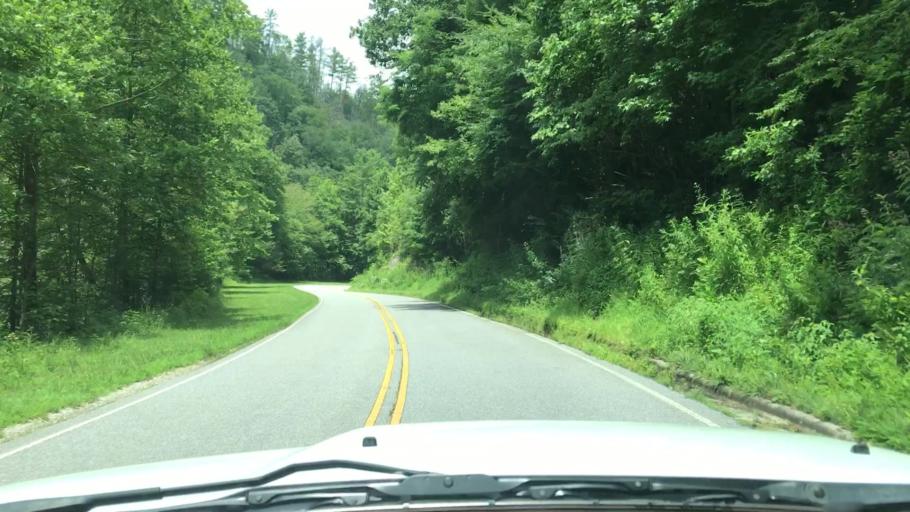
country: US
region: North Carolina
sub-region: Graham County
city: Robbinsville
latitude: 35.4107
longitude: -83.8875
